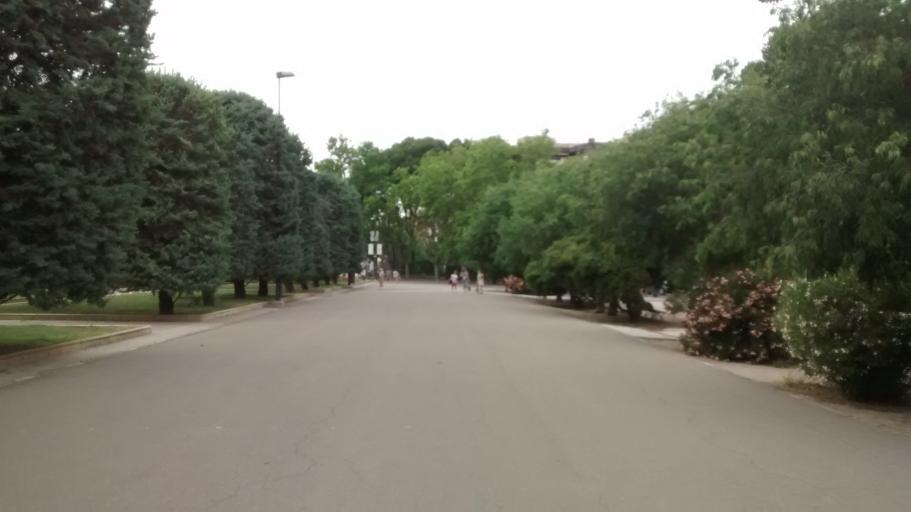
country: ES
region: Aragon
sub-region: Provincia de Zaragoza
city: Delicias
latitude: 41.6361
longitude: -0.8959
